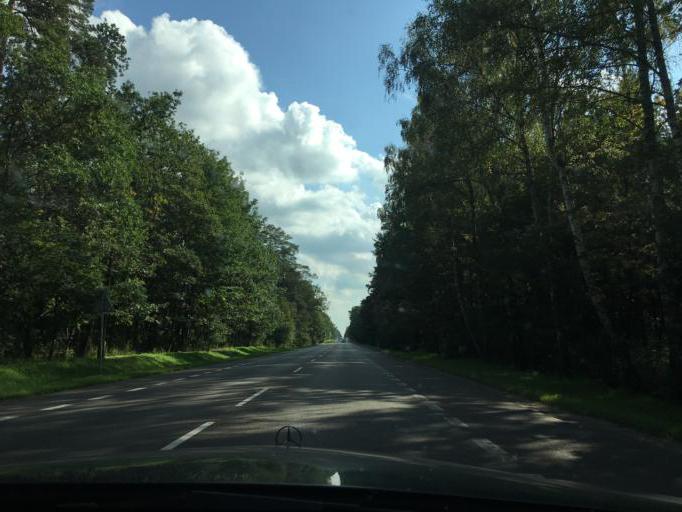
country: PL
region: Podlasie
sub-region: Suwalki
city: Suwalki
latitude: 54.0620
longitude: 22.9349
